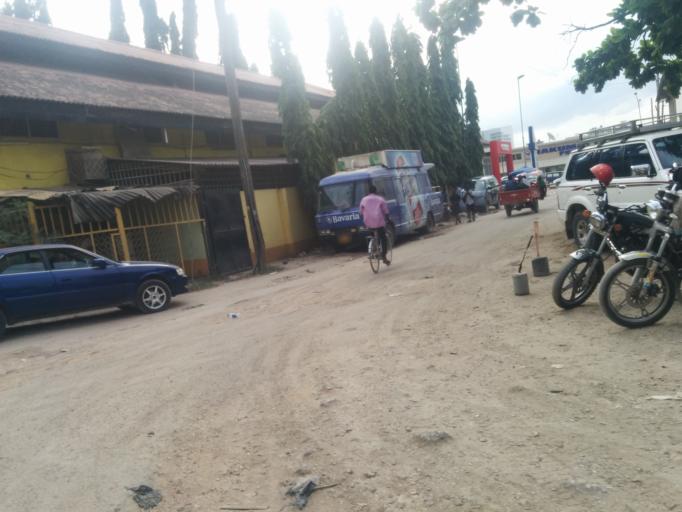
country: TZ
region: Dar es Salaam
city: Dar es Salaam
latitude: -6.8288
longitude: 39.2757
